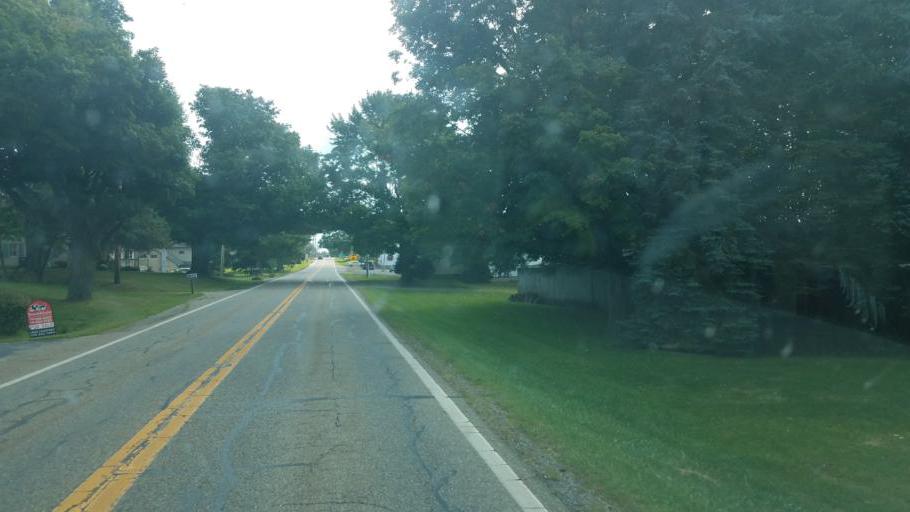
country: US
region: Ohio
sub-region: Columbiana County
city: Salem
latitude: 40.7955
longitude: -80.9298
